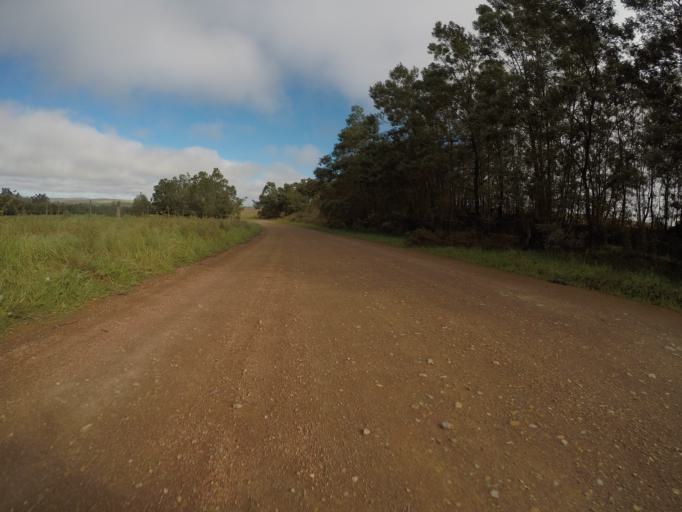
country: ZA
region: Western Cape
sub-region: Overberg District Municipality
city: Caledon
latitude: -34.1137
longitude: 19.7912
